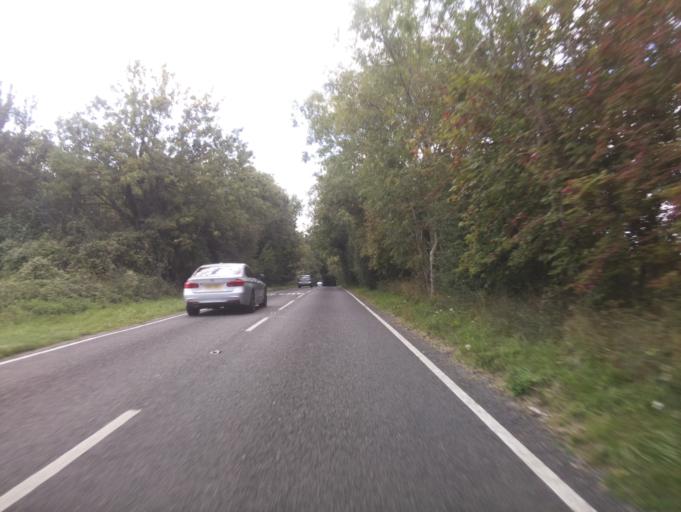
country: GB
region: England
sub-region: Hampshire
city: Abbotts Ann
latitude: 51.1103
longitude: -1.4665
